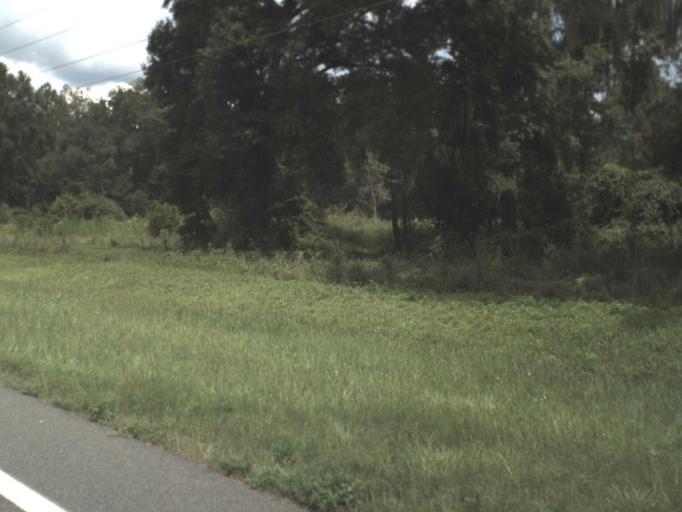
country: US
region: Florida
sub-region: Alachua County
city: Alachua
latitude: 29.8187
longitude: -82.4479
